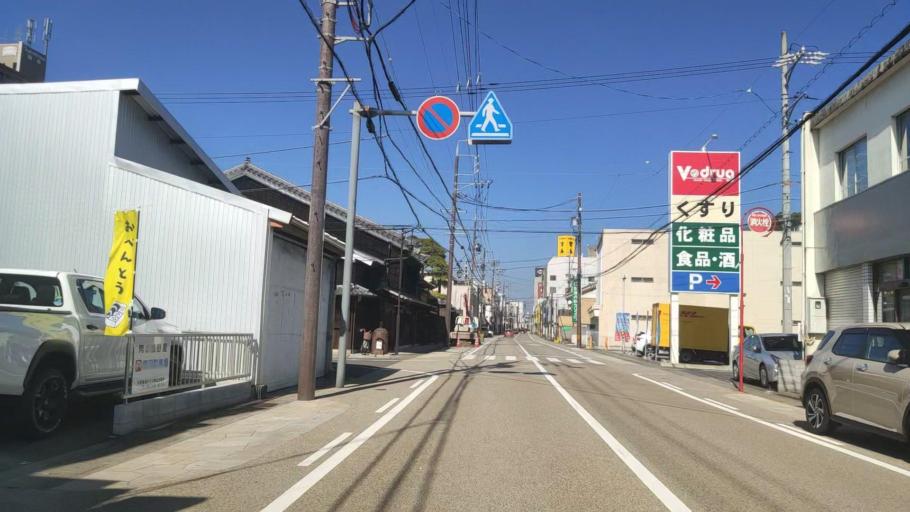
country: JP
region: Gifu
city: Gifu-shi
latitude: 35.4224
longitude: 136.7634
